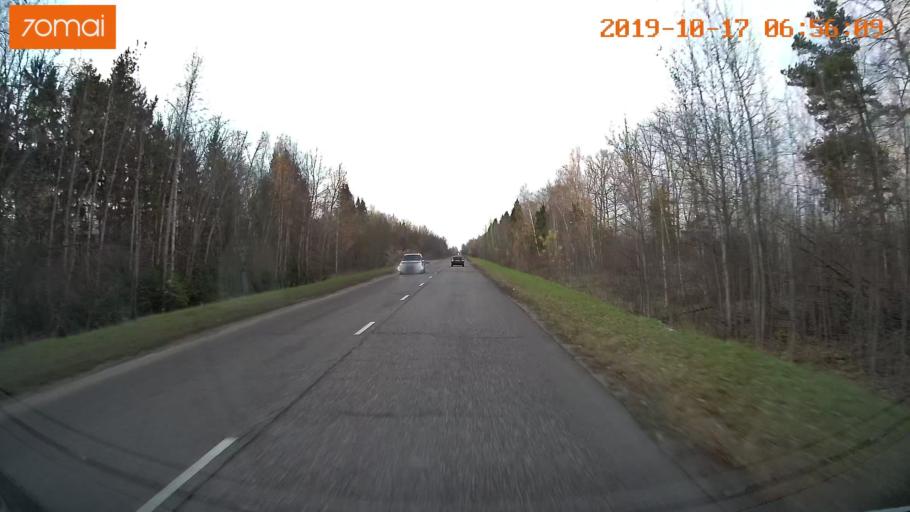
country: RU
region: Vladimir
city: Suzdal'
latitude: 56.4495
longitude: 40.4502
